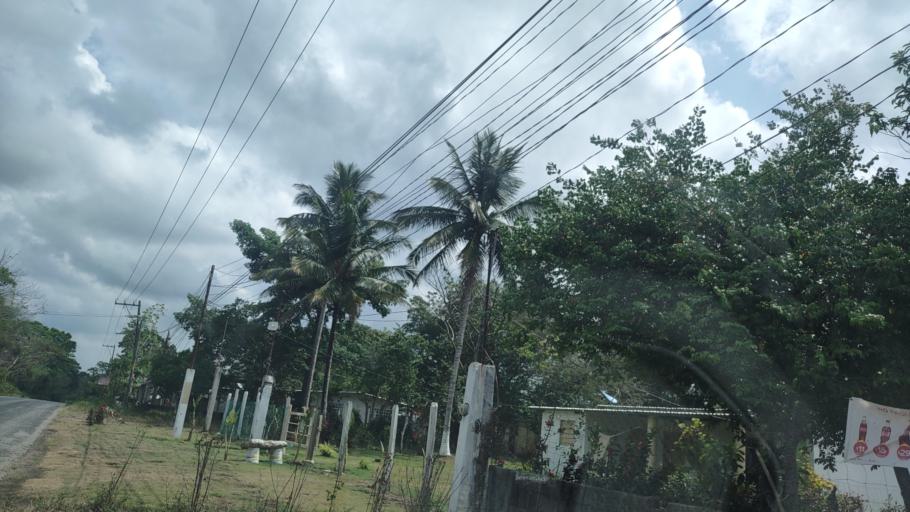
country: MX
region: Veracruz
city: Las Choapas
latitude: 17.9505
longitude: -94.1099
